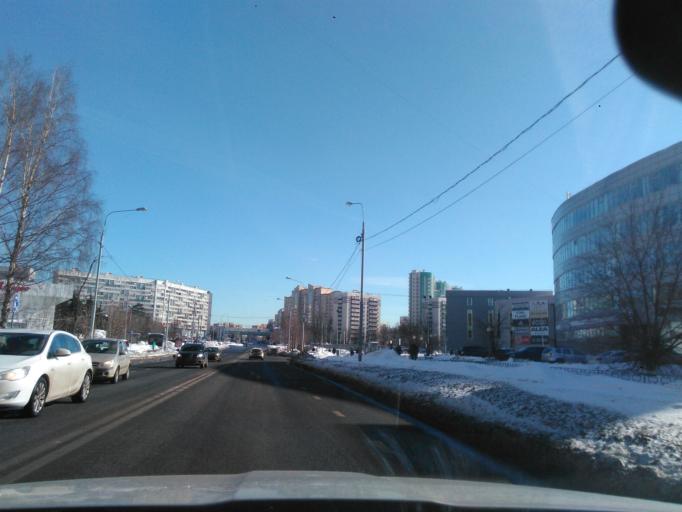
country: RU
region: Moscow
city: Zelenograd
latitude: 55.9842
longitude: 37.1737
